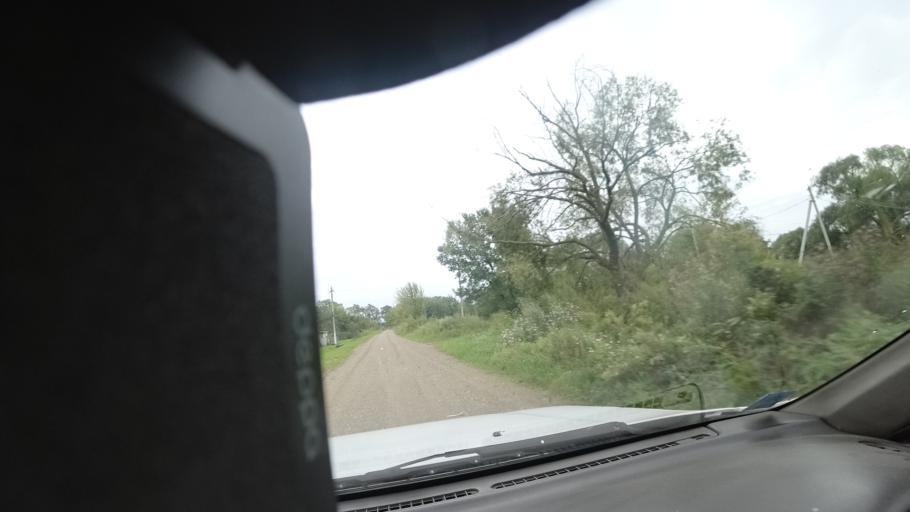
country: RU
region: Primorskiy
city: Lazo
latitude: 45.8302
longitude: 133.6135
